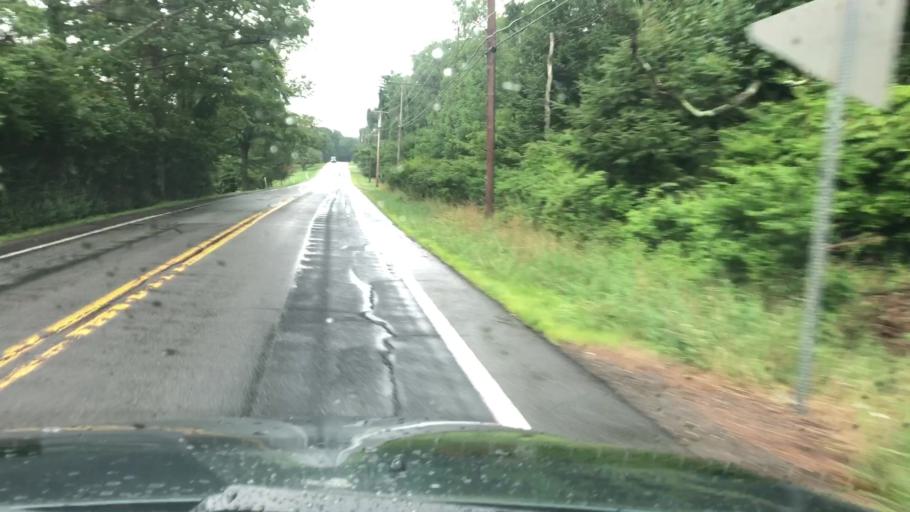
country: US
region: Pennsylvania
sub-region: Monroe County
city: Mountainhome
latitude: 41.2230
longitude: -75.2335
